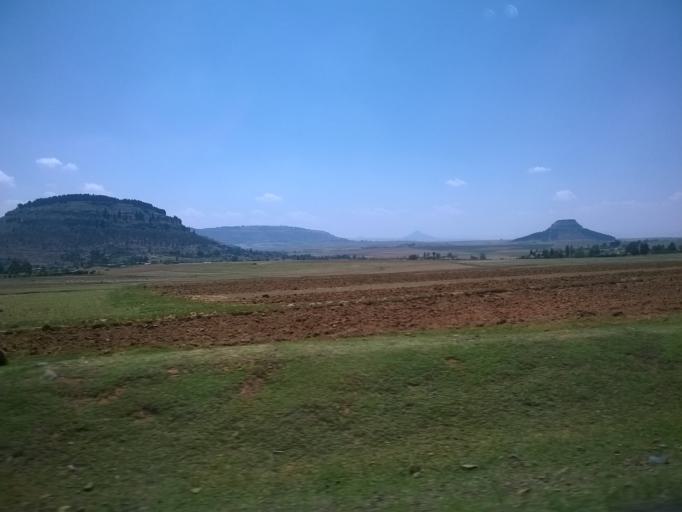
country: LS
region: Leribe
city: Maputsoe
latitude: -28.9666
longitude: 27.9640
